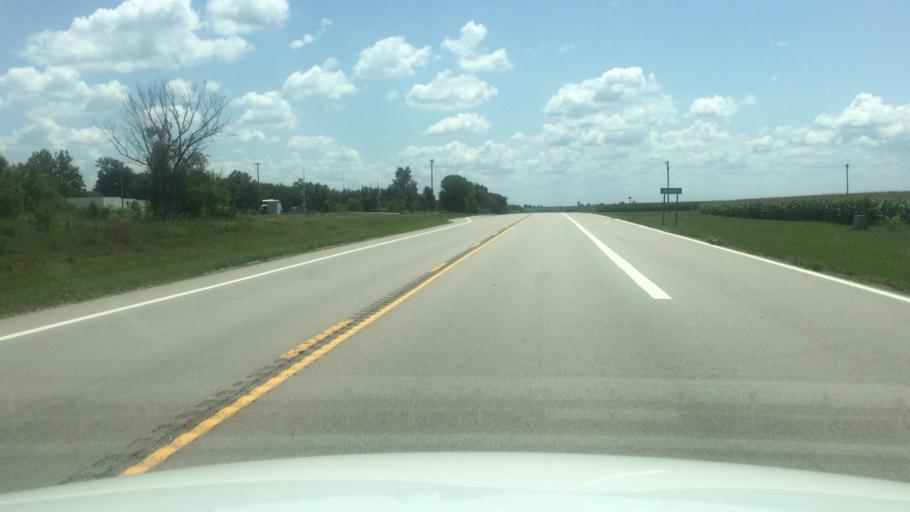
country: US
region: Kansas
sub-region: Brown County
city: Horton
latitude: 39.6397
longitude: -95.3537
